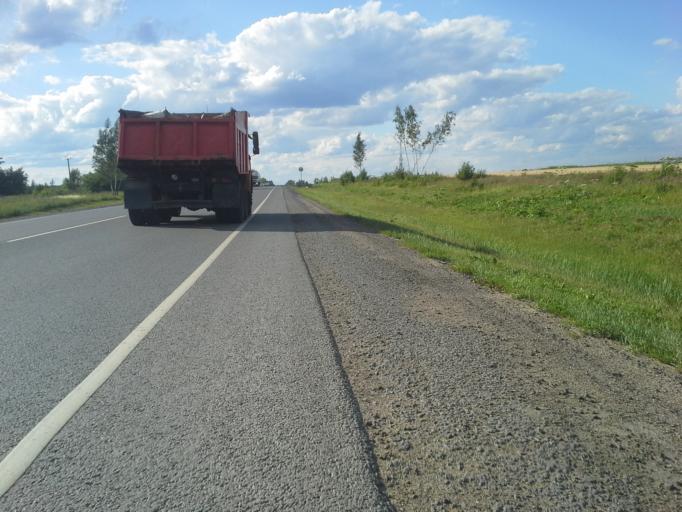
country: RU
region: Moskovskaya
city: Klimovsk
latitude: 55.3557
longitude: 37.4397
